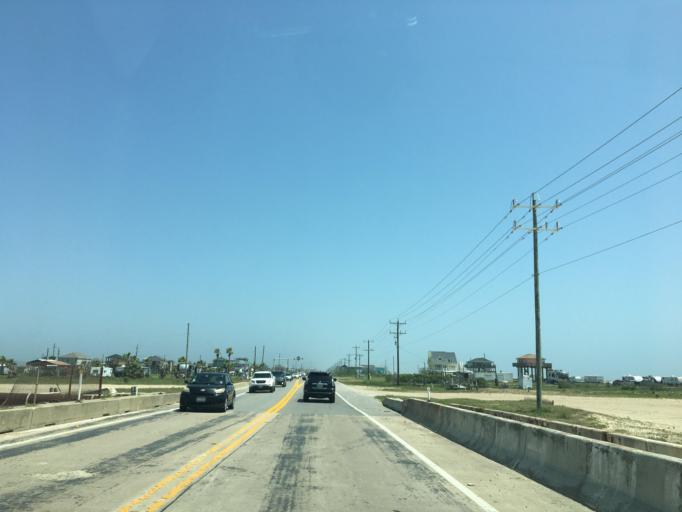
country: US
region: Texas
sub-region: Galveston County
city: Bolivar Peninsula
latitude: 29.5084
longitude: -94.5003
